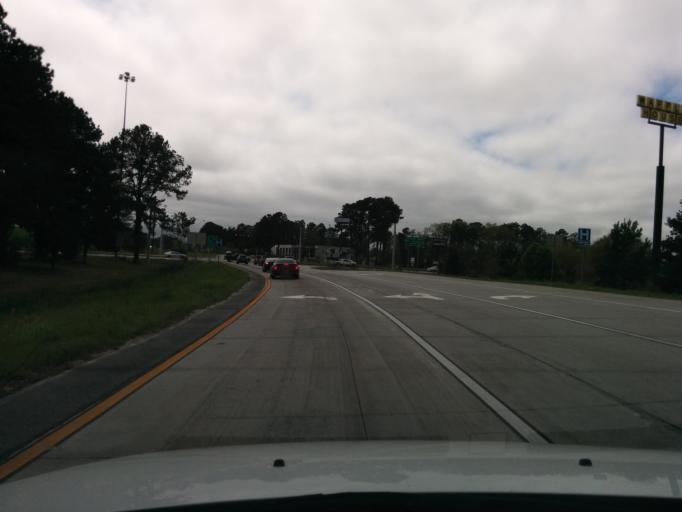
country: US
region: Georgia
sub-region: Chatham County
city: Georgetown
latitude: 32.0060
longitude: -81.2834
